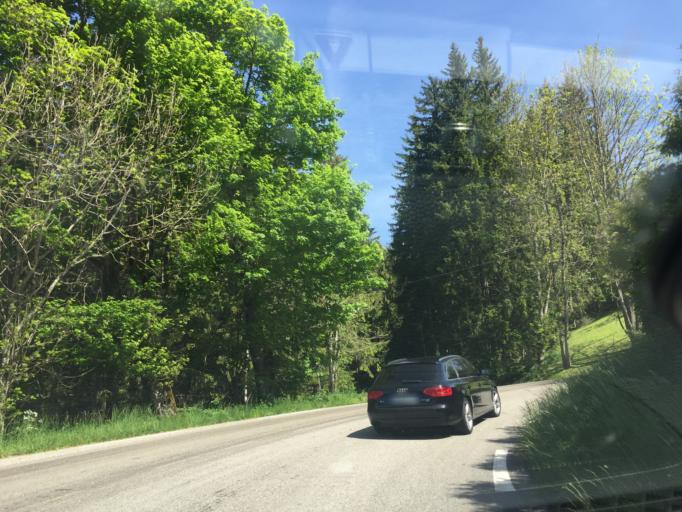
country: FR
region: Rhone-Alpes
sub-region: Departement de l'Isere
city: Saint-Hilaire
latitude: 45.3410
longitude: 5.8119
